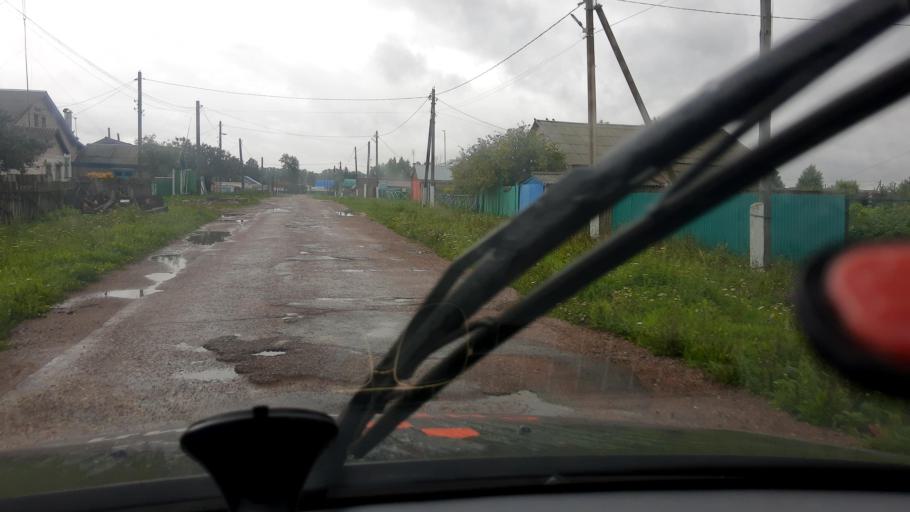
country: RU
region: Bashkortostan
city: Karmaskaly
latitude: 53.9898
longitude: 56.3954
